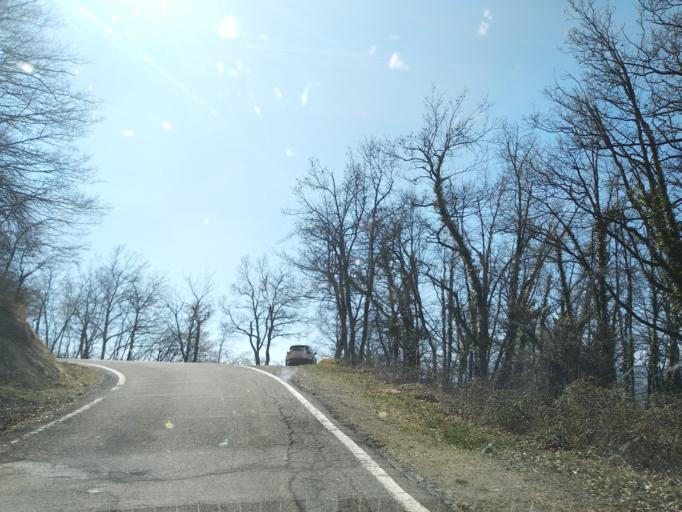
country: IT
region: Emilia-Romagna
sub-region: Provincia di Reggio Emilia
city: Castelnovo ne'Monti
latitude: 44.4219
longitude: 10.4067
